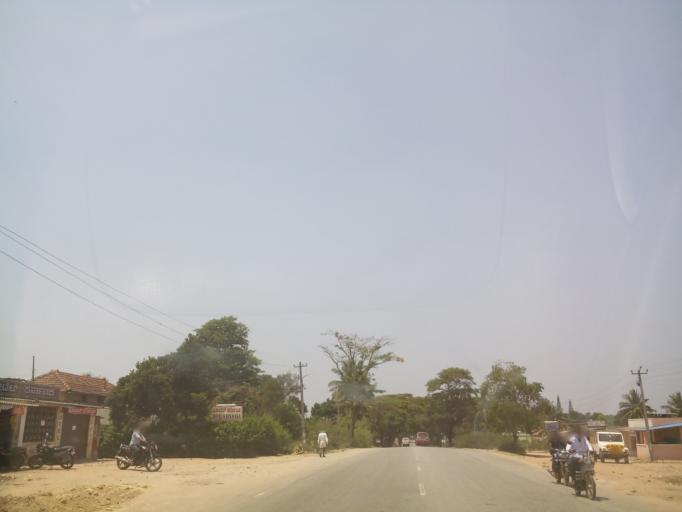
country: IN
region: Karnataka
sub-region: Hassan
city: Alur
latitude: 12.9449
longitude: 75.8909
